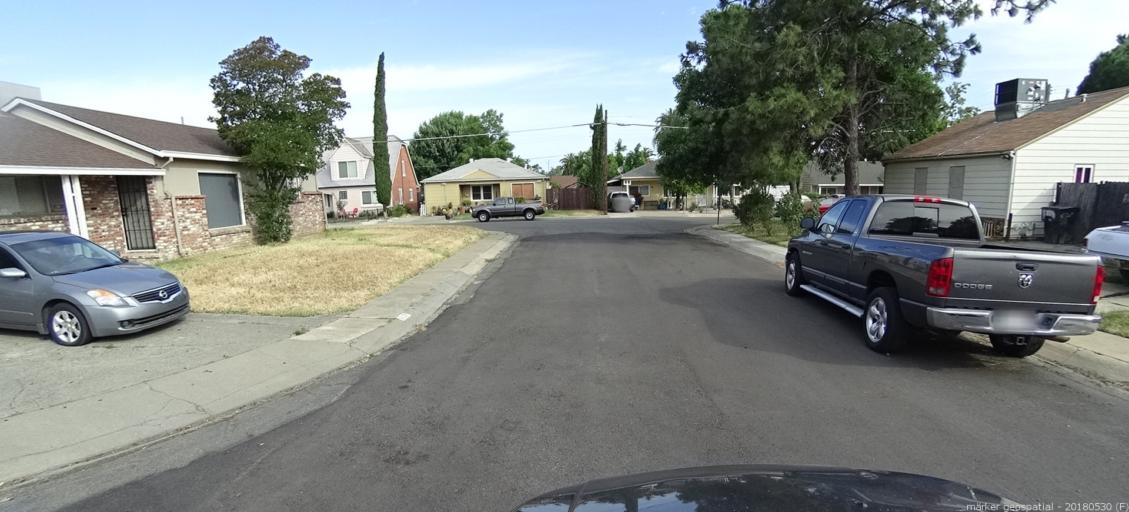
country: US
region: California
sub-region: Sacramento County
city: Sacramento
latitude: 38.6137
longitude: -121.4433
